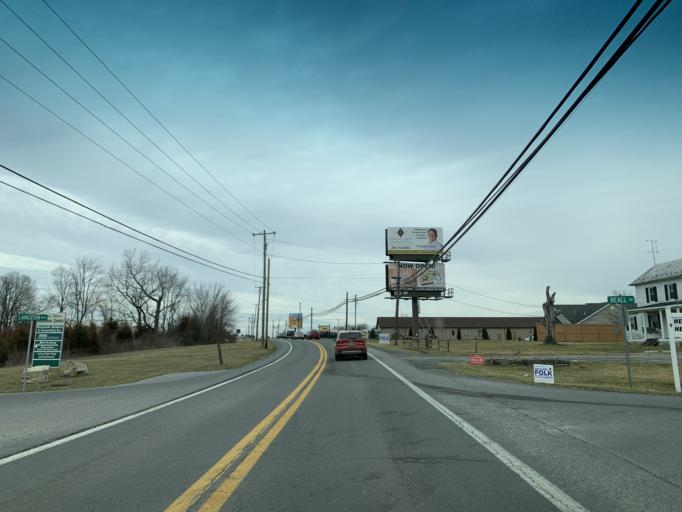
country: US
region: West Virginia
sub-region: Berkeley County
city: Martinsburg
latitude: 39.5346
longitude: -77.9112
